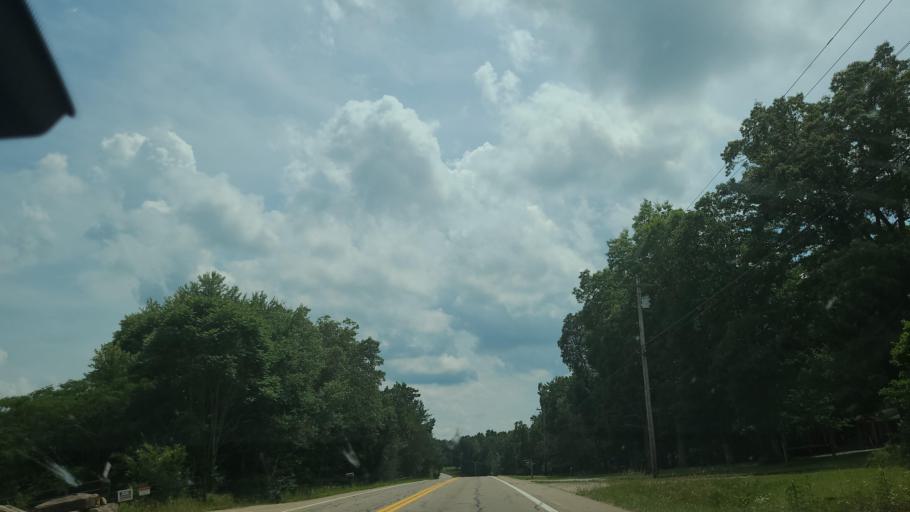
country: US
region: Tennessee
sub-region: Cumberland County
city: Lake Tansi
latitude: 35.8432
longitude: -85.0167
